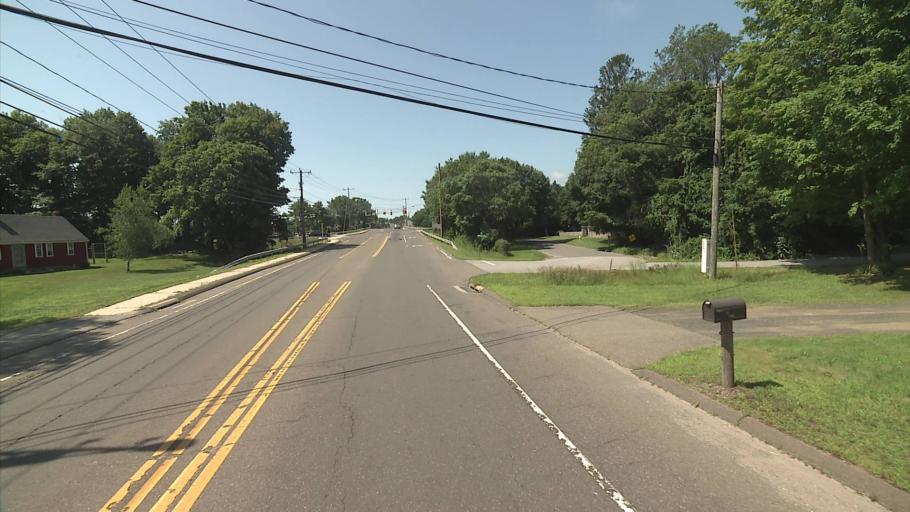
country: US
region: Connecticut
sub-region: Middlesex County
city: Westbrook Center
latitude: 41.2931
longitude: -72.4421
